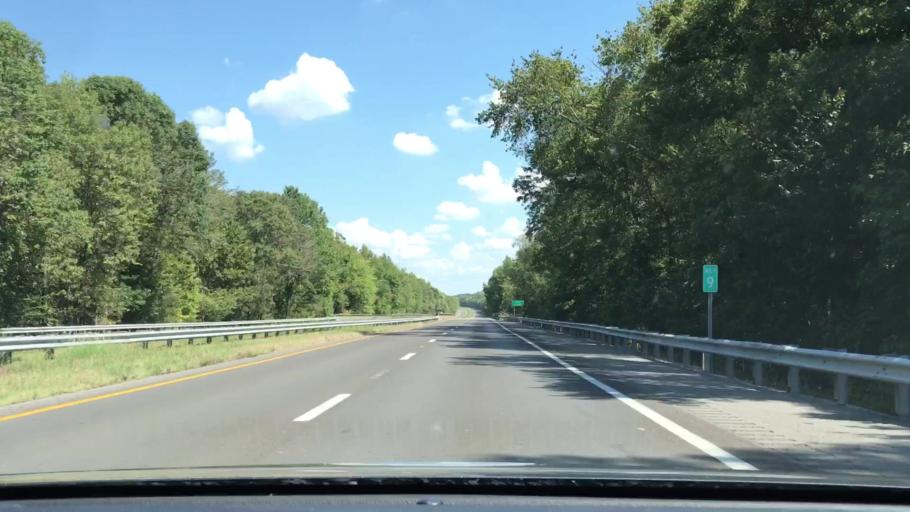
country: US
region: Kentucky
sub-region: Fulton County
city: Fulton
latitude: 36.5948
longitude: -88.8082
